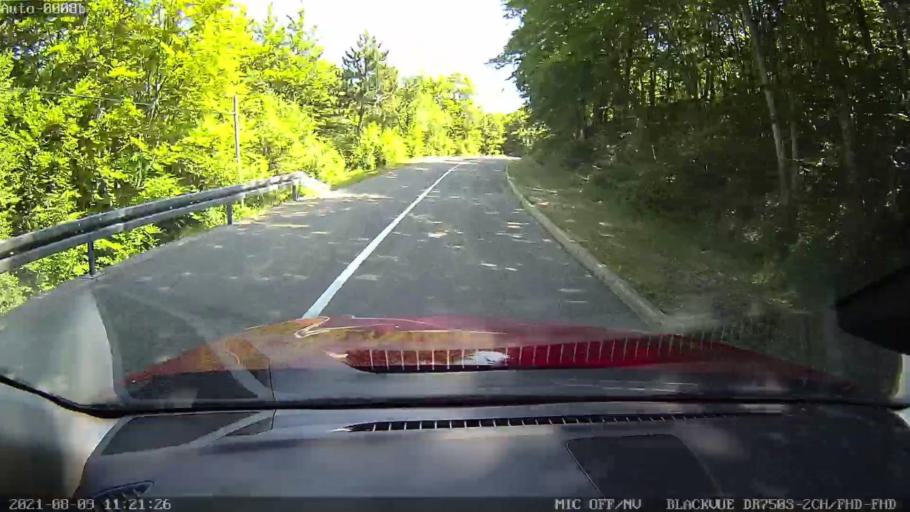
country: HR
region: Istarska
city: Lovran
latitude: 45.3040
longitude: 14.2005
